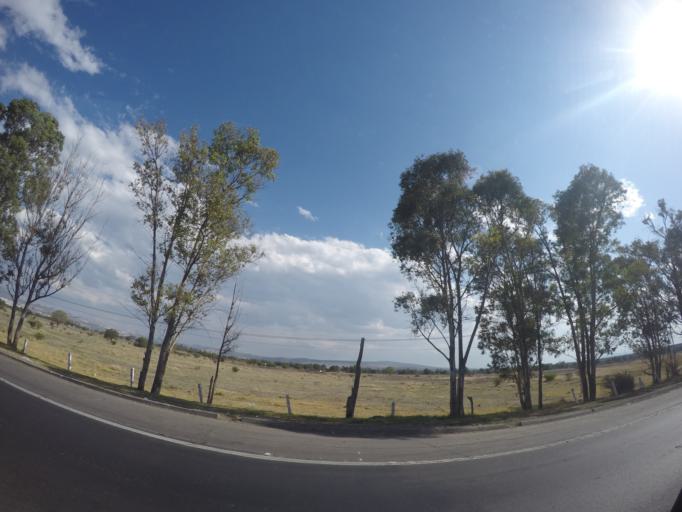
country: MX
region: Guanajuato
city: El Castillo
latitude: 20.5731
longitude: -100.4649
